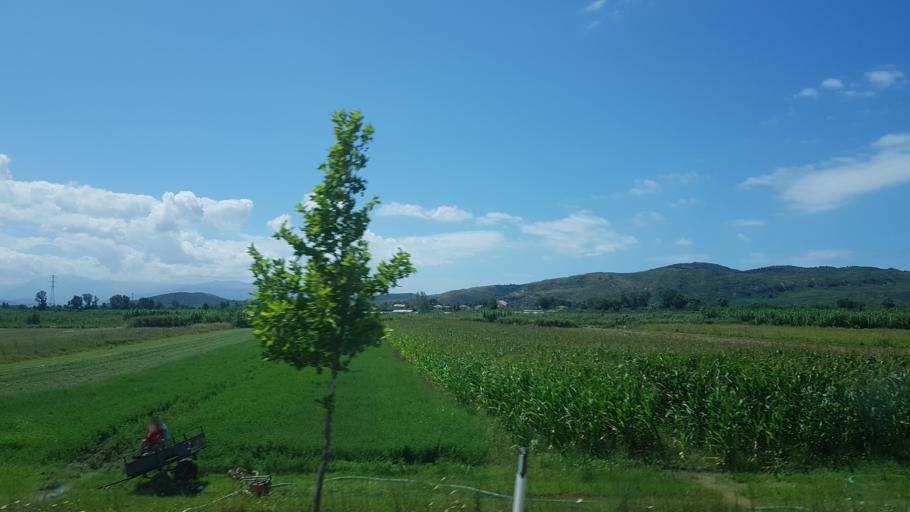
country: AL
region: Fier
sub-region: Rrethi i Fierit
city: Frakulla e Madhe
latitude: 40.6061
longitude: 19.5439
